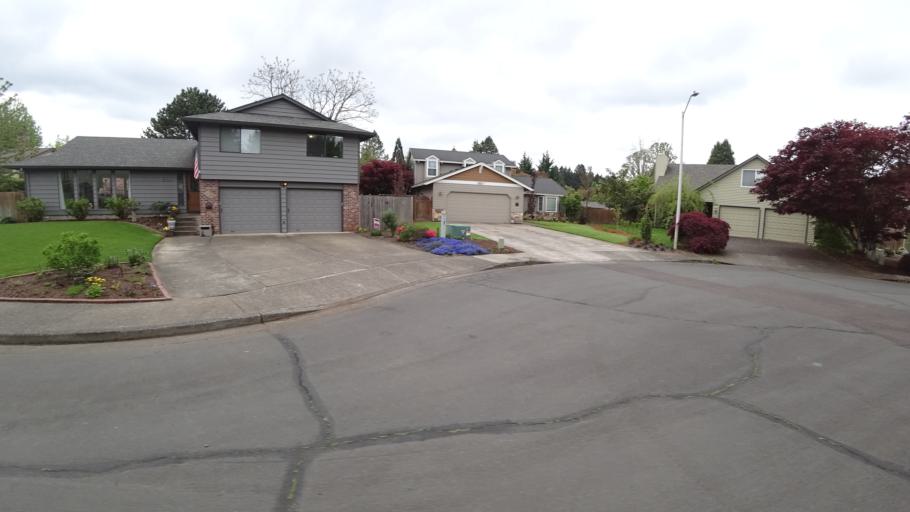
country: US
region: Oregon
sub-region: Washington County
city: Hillsboro
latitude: 45.5401
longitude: -122.9854
